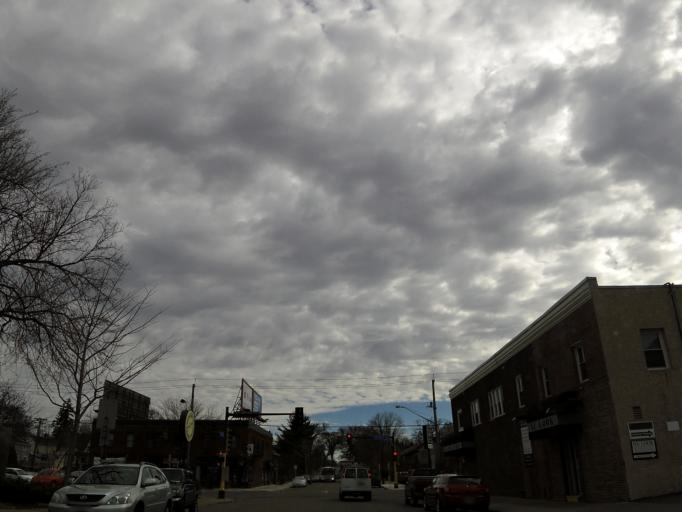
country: US
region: Minnesota
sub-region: Hennepin County
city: Richfield
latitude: 44.9129
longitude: -93.3087
